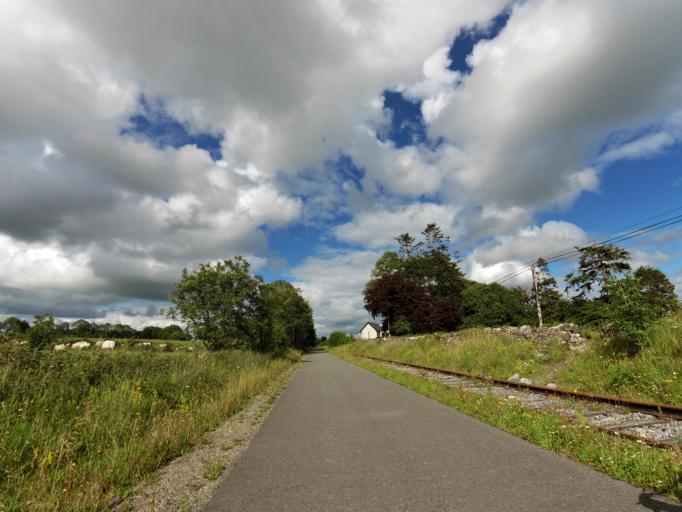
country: IE
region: Leinster
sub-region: An Iarmhi
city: Kilbeggan
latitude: 53.4492
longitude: -7.5330
